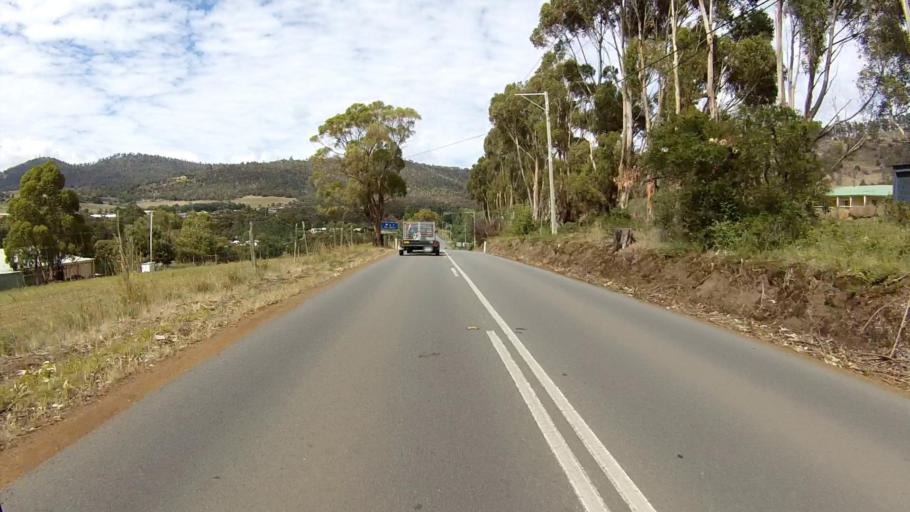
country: AU
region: Tasmania
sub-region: Clarence
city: Cambridge
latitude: -42.8292
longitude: 147.4467
